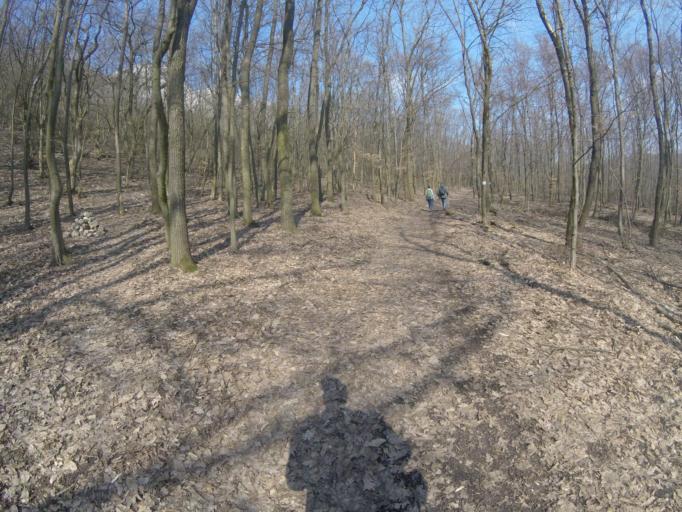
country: HU
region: Komarom-Esztergom
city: Nyergesujfalu
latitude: 47.7258
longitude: 18.5754
